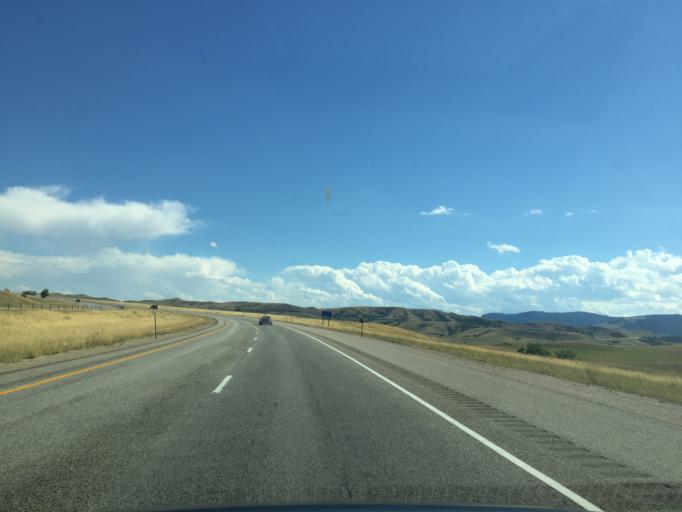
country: US
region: Wyoming
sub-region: Sheridan County
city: Sheridan
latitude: 44.6065
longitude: -106.8481
